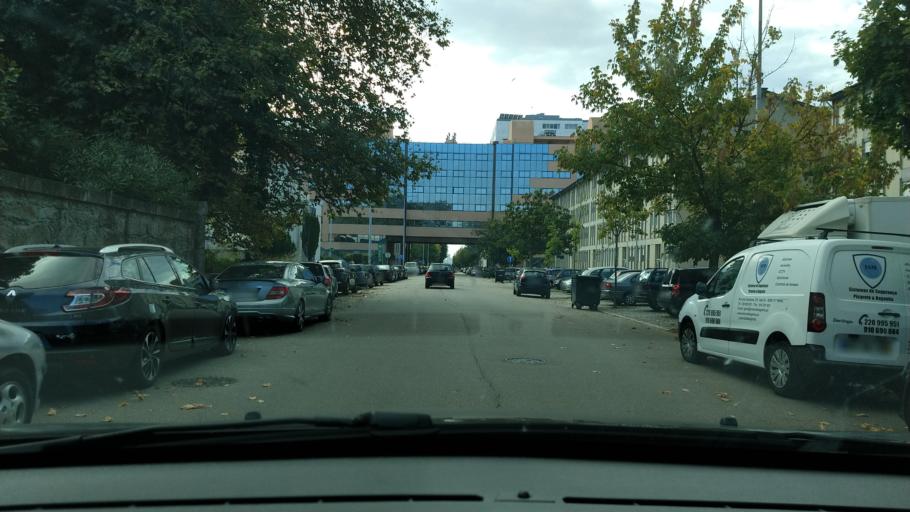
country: PT
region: Porto
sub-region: Porto
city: Porto
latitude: 41.1650
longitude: -8.5975
